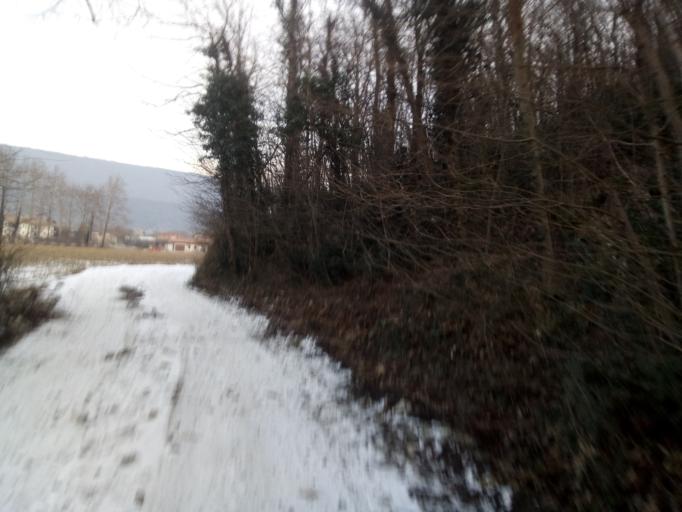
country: IT
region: Piedmont
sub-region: Provincia di Torino
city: Cascinette d'Ivrea
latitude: 45.4808
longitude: 7.9009
